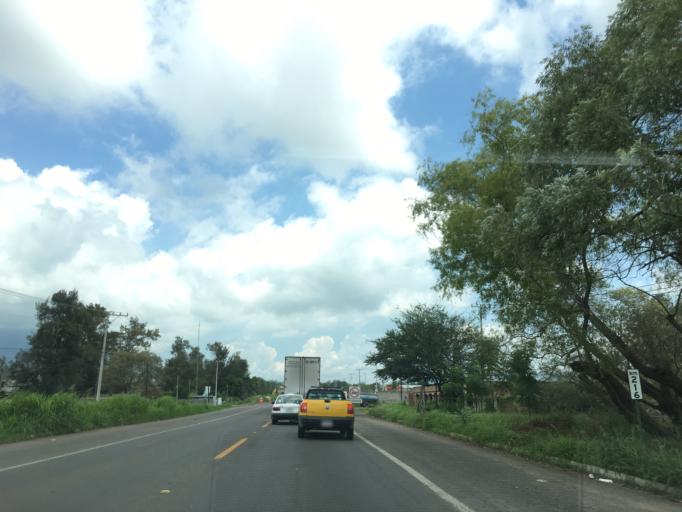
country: MX
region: Nayarit
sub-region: Tepic
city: La Corregidora
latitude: 21.4576
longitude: -104.8248
